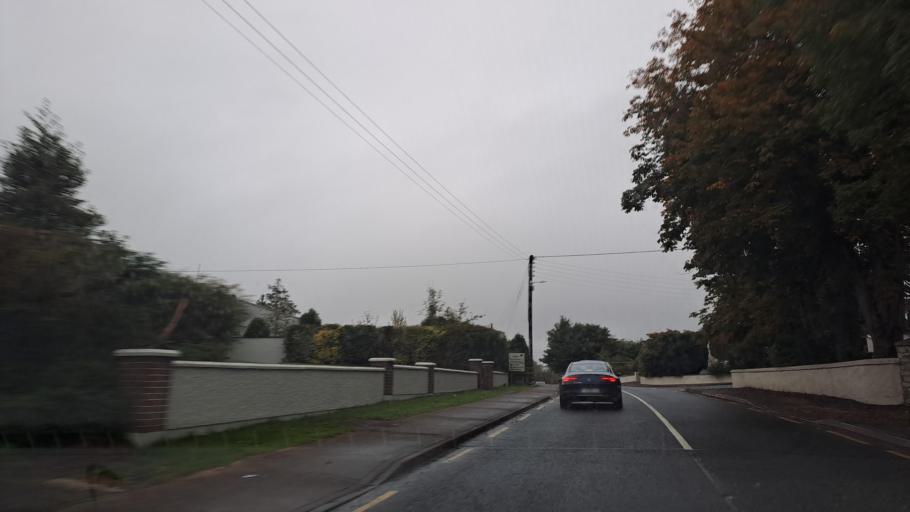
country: IE
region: Ulster
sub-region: County Monaghan
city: Monaghan
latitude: 54.2359
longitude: -6.9650
